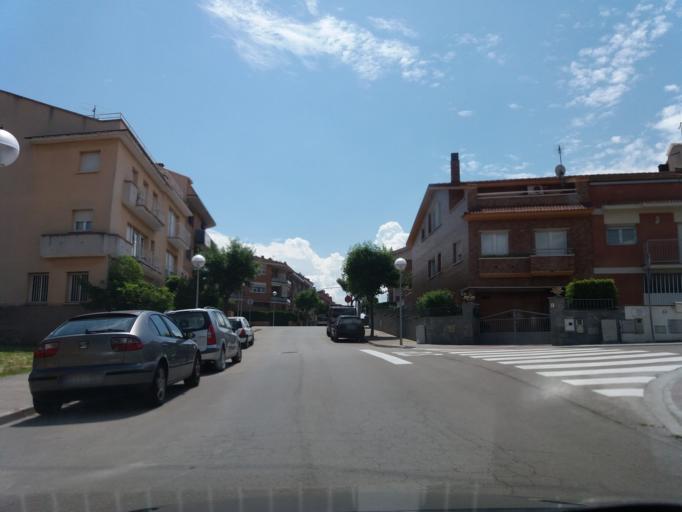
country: ES
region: Catalonia
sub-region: Provincia de Barcelona
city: Sant Joan de Vilatorrada
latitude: 41.7388
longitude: 1.7989
